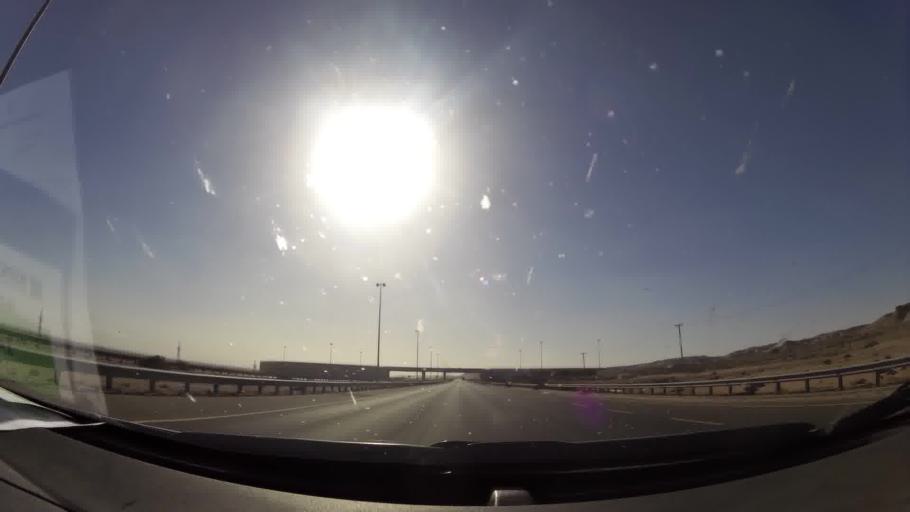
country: KW
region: Al Asimah
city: Kuwait City
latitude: 29.5242
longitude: 47.8167
